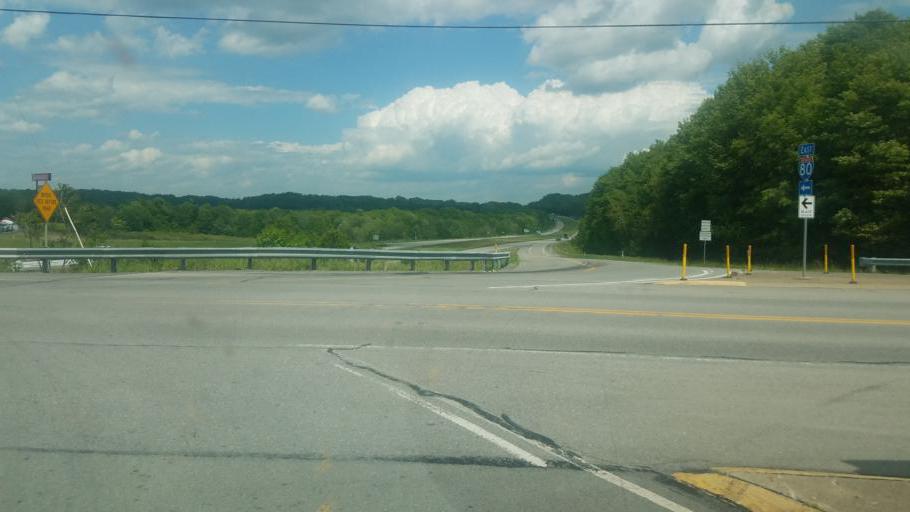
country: US
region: Pennsylvania
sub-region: Venango County
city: Franklin
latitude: 41.1892
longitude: -79.8689
